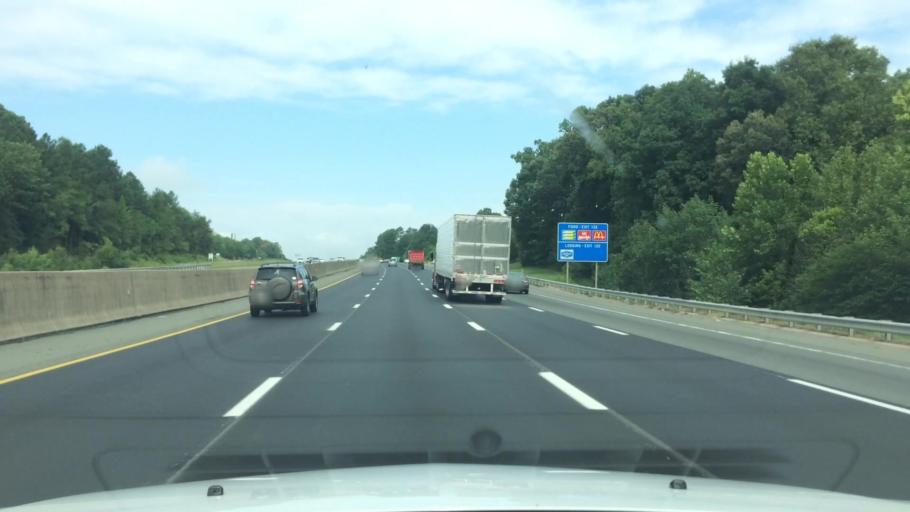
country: US
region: North Carolina
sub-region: Guilford County
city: McLeansville
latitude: 36.0585
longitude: -79.6415
